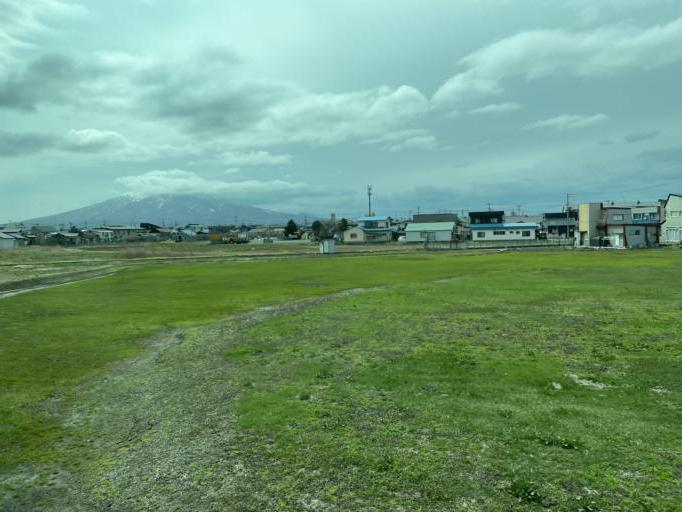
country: JP
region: Aomori
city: Goshogawara
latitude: 40.7613
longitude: 140.4356
